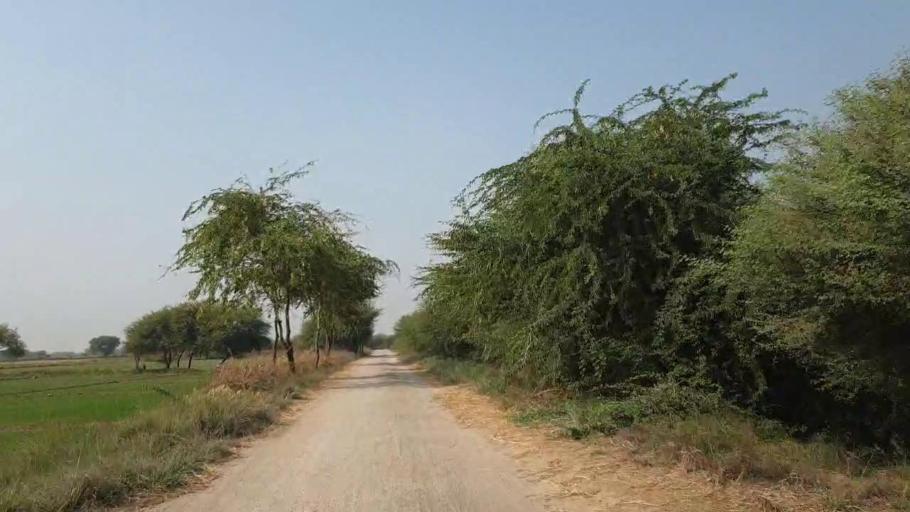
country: PK
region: Sindh
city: Kario
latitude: 24.9410
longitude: 68.5369
